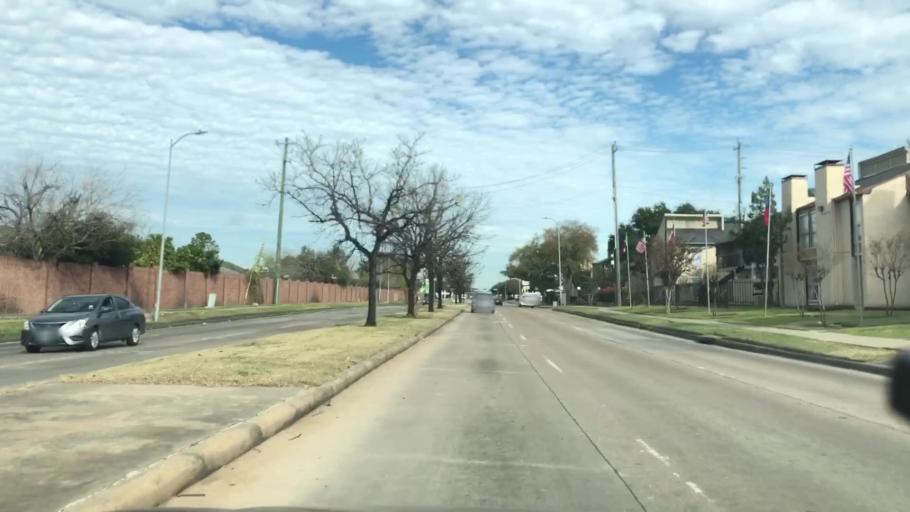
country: US
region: Texas
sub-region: Fort Bend County
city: Missouri City
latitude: 29.6521
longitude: -95.5083
